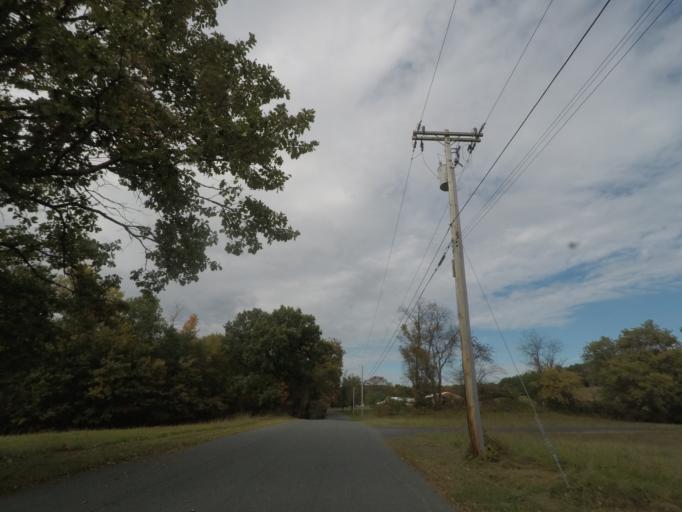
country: US
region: New York
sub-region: Rensselaer County
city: Nassau
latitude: 42.5478
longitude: -73.6243
